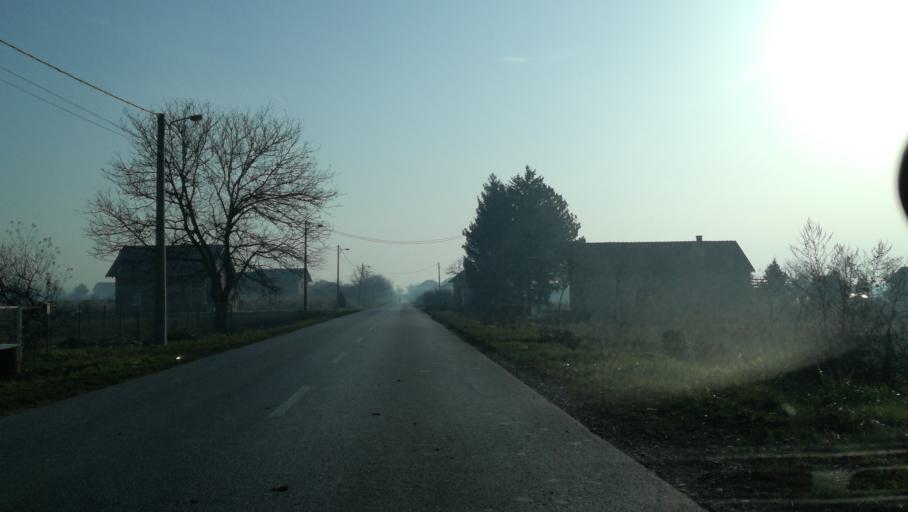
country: RS
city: Prislonica
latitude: 43.9006
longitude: 20.4096
